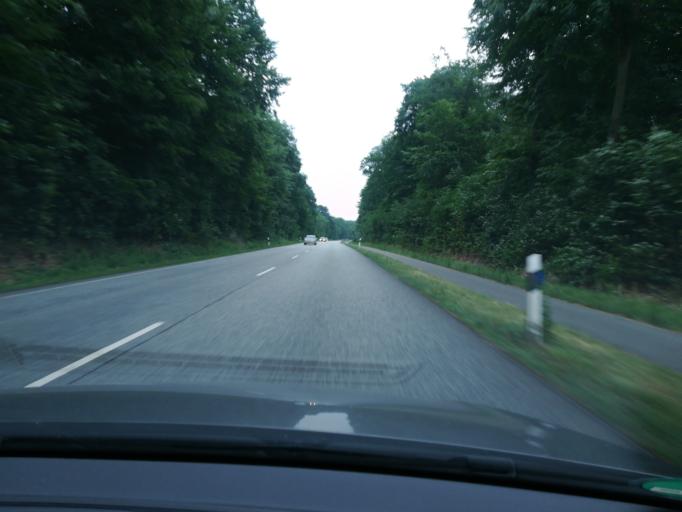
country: DE
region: Schleswig-Holstein
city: Brunstorf
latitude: 53.5275
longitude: 10.4400
